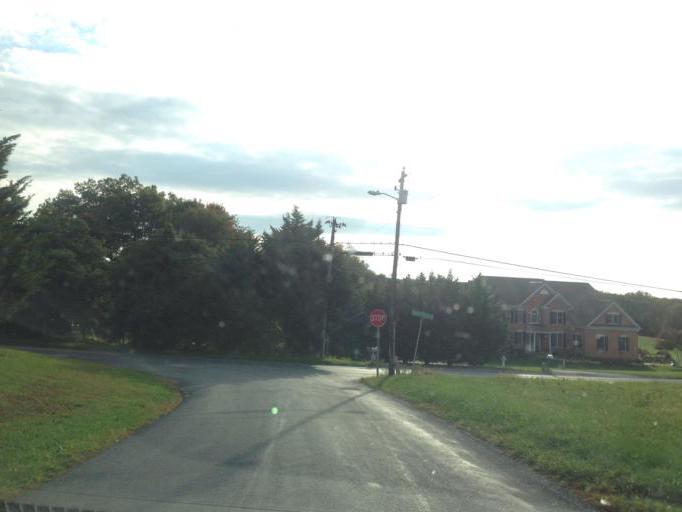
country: US
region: Maryland
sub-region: Carroll County
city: Mount Airy
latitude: 39.3297
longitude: -77.1577
